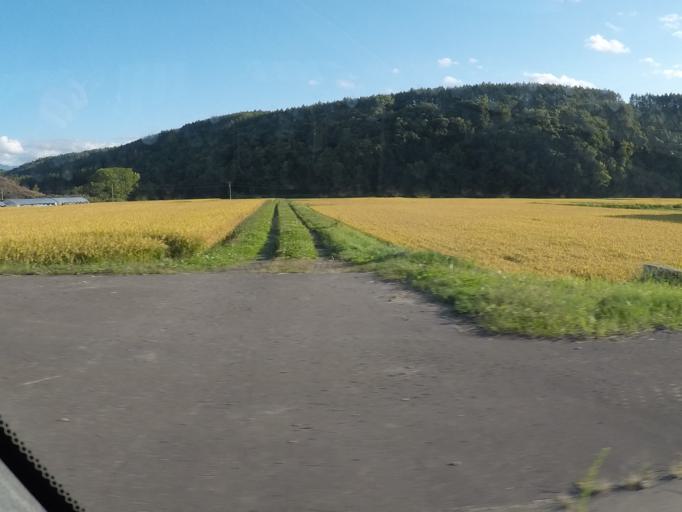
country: JP
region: Hokkaido
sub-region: Asahikawa-shi
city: Asahikawa
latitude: 43.6268
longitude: 142.5409
